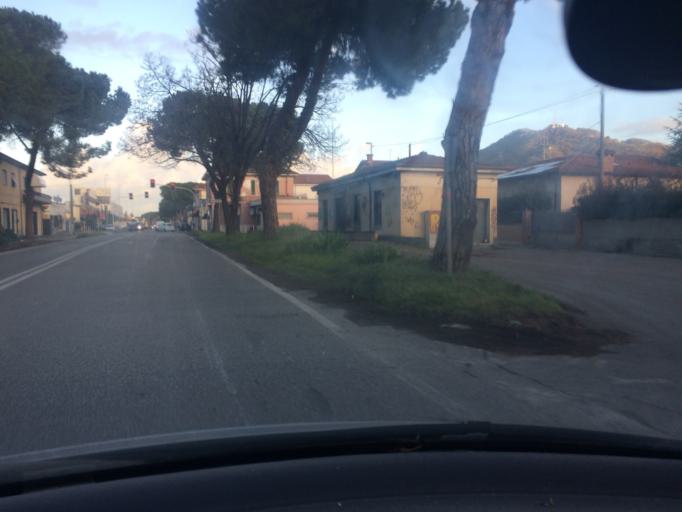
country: IT
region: Tuscany
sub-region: Provincia di Massa-Carrara
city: Carrara
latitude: 44.0513
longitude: 10.0721
